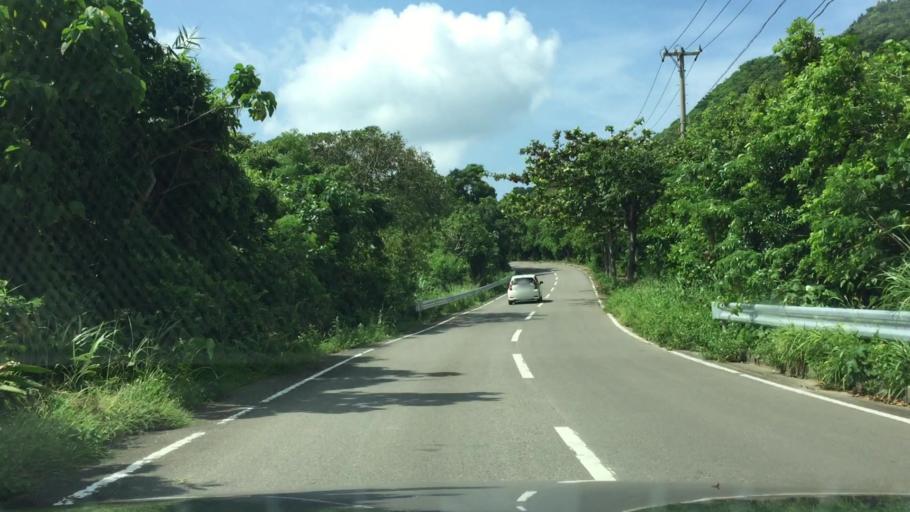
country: JP
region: Okinawa
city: Ishigaki
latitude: 24.4674
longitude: 124.2256
